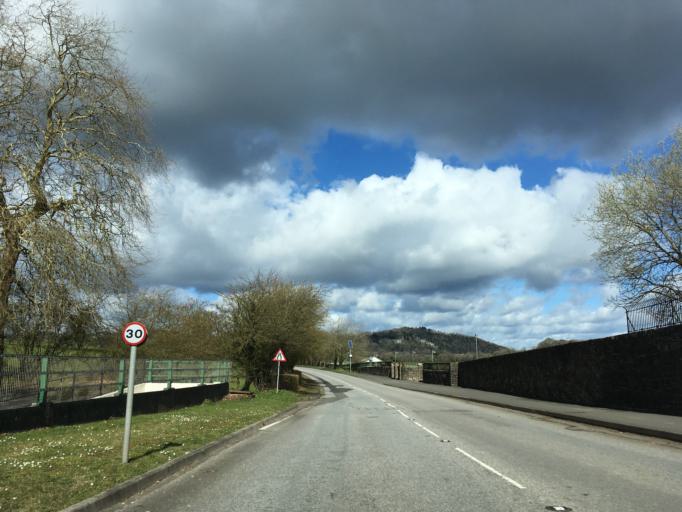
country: GB
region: Wales
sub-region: Monmouthshire
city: Chepstow
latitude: 51.6528
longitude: -2.6925
